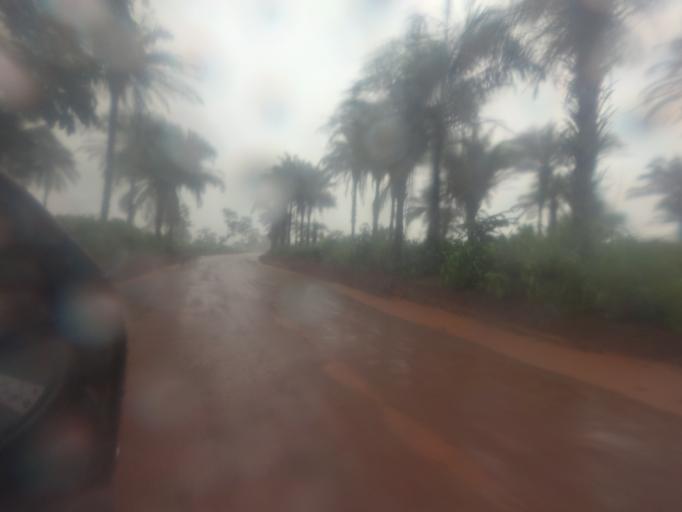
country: SL
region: Northern Province
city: Kambia
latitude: 9.2253
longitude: -12.8355
